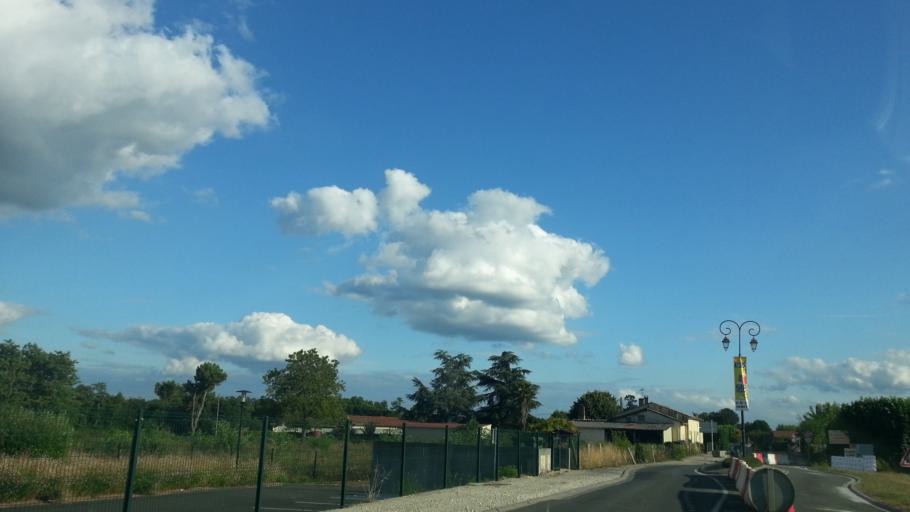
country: FR
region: Aquitaine
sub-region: Departement de la Gironde
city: Illats
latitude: 44.6022
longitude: -0.3702
